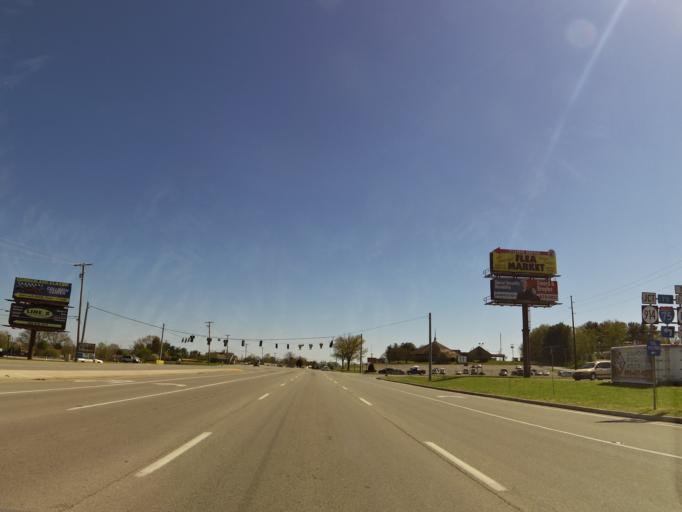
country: US
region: Kentucky
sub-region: Pulaski County
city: Somerset
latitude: 37.0303
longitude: -84.6272
